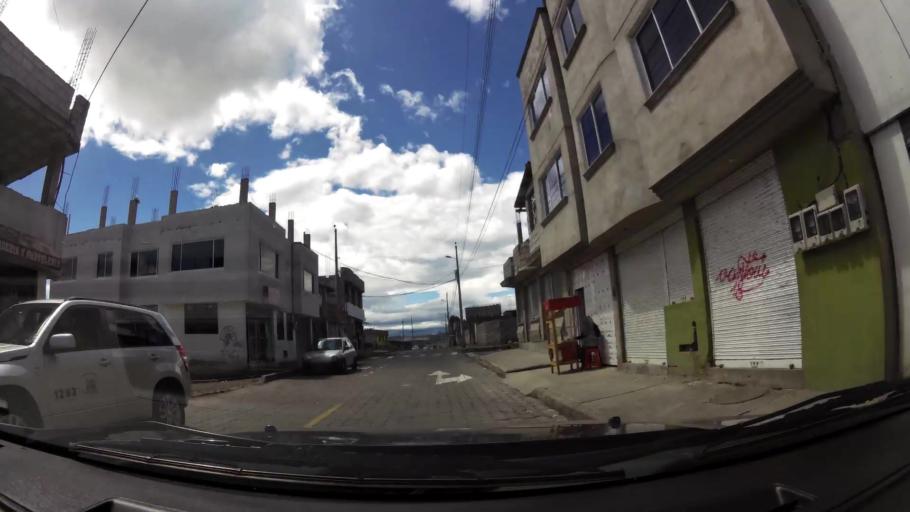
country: EC
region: Pichincha
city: Quito
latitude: -0.3259
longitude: -78.5608
